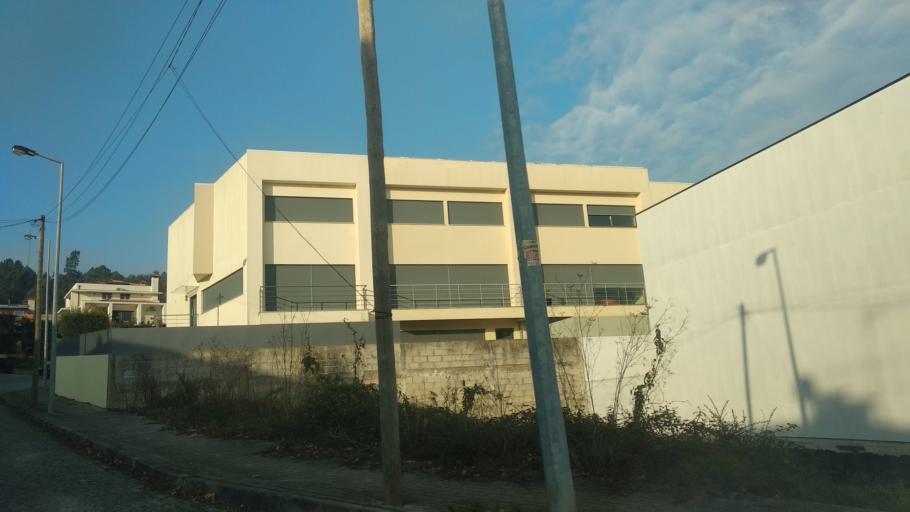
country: PT
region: Braga
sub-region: Braga
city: Adaufe
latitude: 41.5722
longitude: -8.3794
